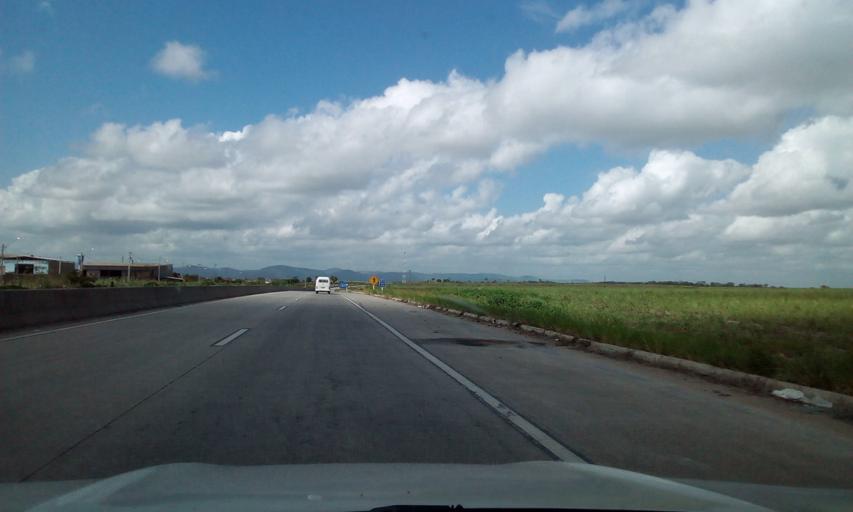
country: BR
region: Alagoas
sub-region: Messias
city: Messias
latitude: -9.3990
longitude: -35.8365
